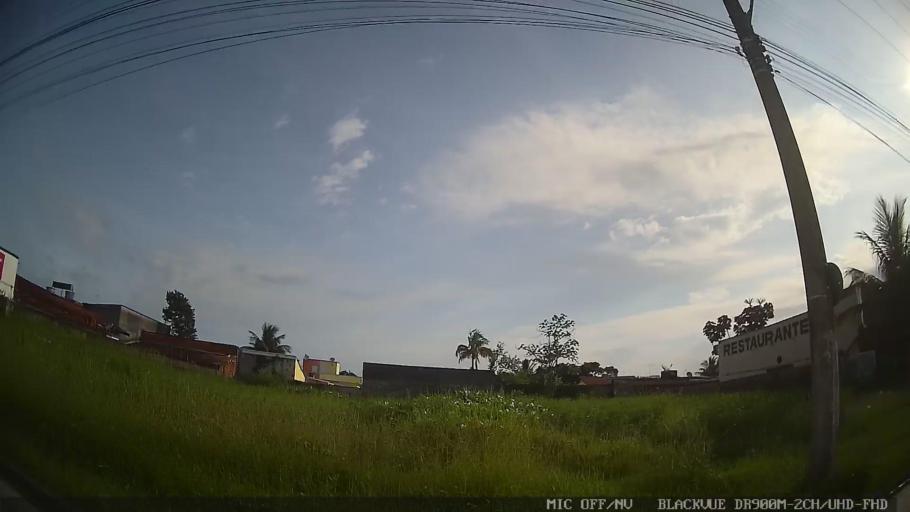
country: BR
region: Sao Paulo
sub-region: Bertioga
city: Bertioga
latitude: -23.8063
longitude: -46.0577
